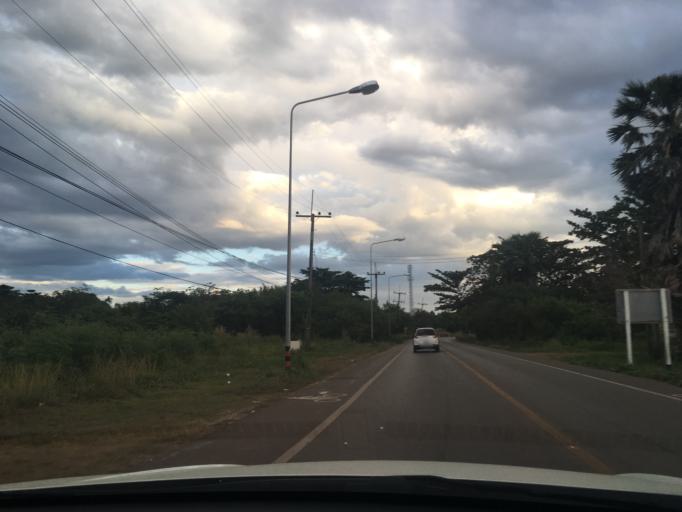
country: TH
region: Chanthaburi
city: Na Yai Am
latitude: 12.6441
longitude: 101.8614
